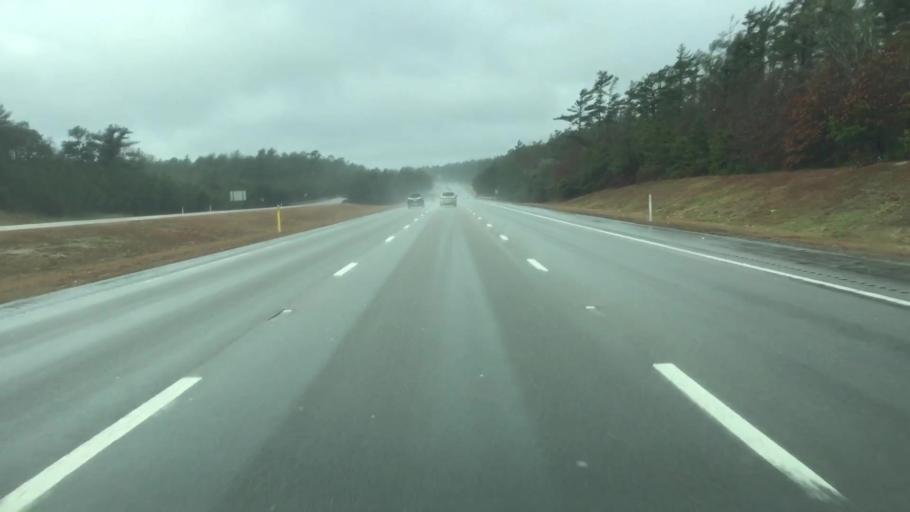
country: US
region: Massachusetts
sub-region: Plymouth County
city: White Island Shores
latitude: 41.7780
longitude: -70.6277
